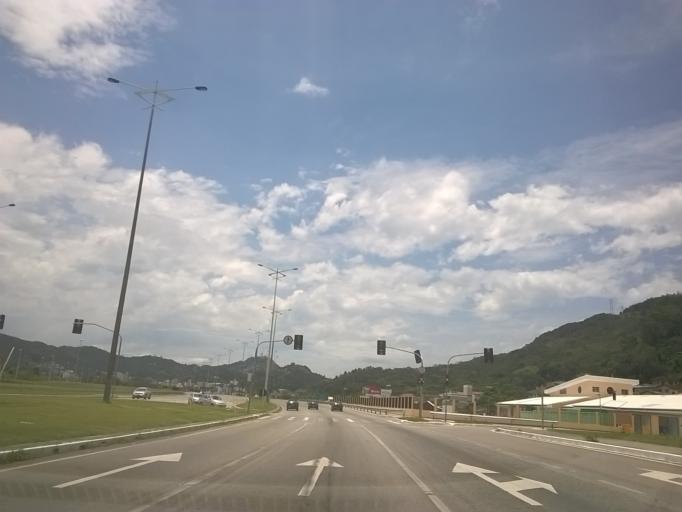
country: BR
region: Santa Catarina
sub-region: Florianopolis
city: Costeira do Pirajubae
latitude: -27.6288
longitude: -48.5265
